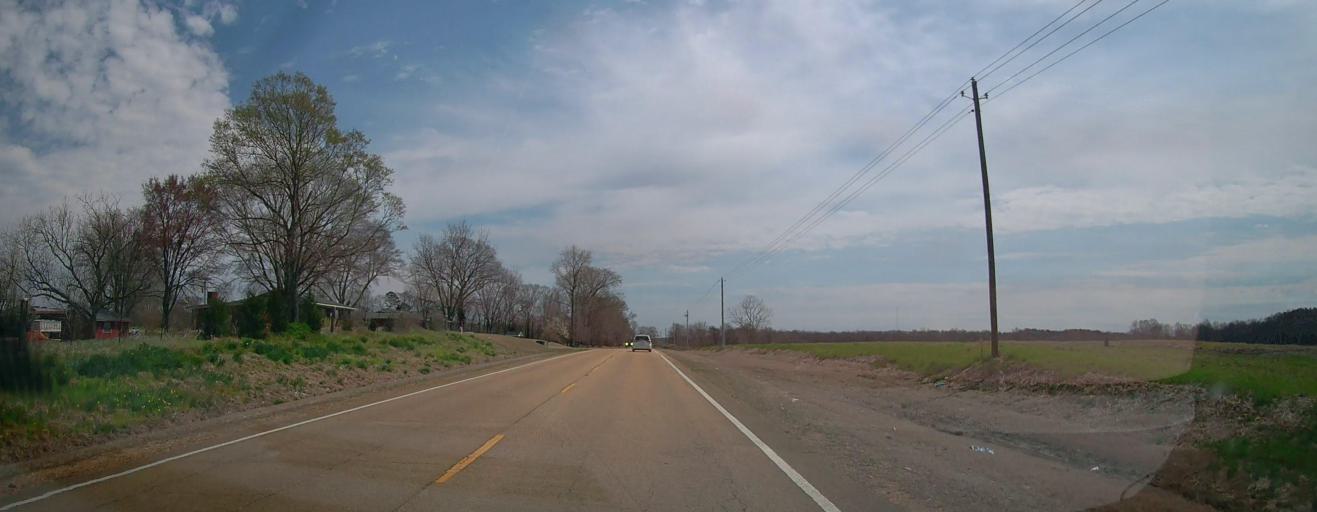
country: US
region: Mississippi
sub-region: Benton County
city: Ashland
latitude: 34.6210
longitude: -89.2318
